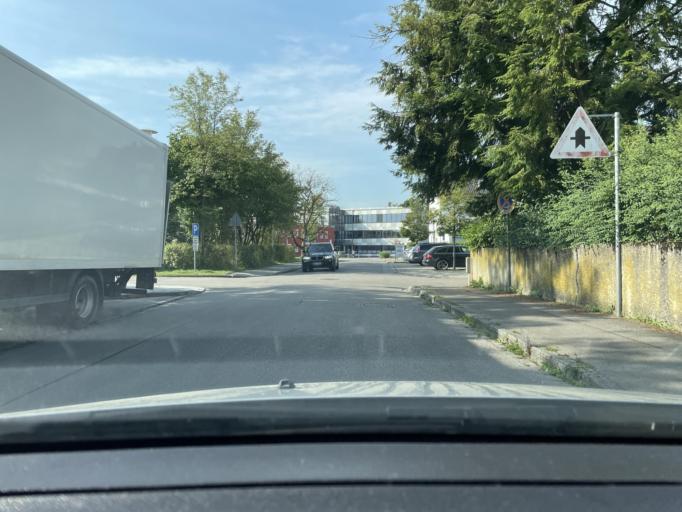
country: DE
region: Bavaria
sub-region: Upper Bavaria
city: Muehldorf
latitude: 48.2455
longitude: 12.5270
